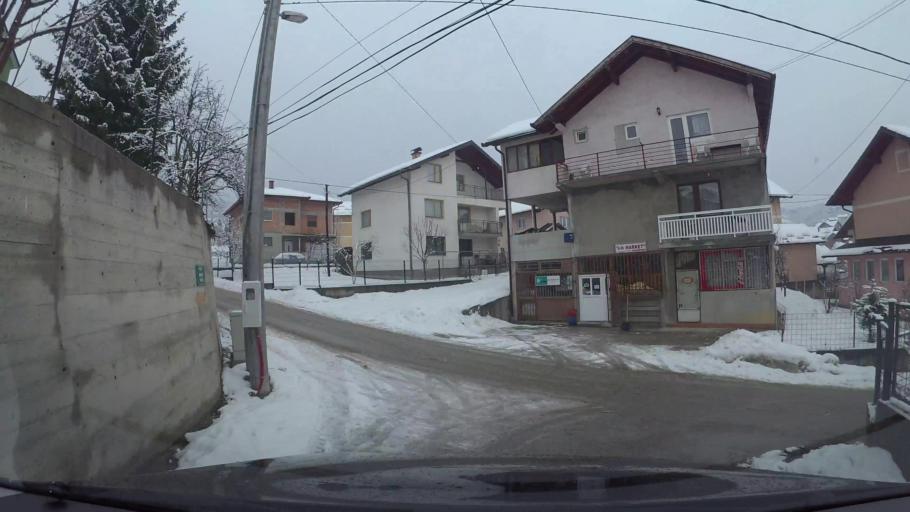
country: BA
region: Federation of Bosnia and Herzegovina
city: Vogosca
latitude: 43.8753
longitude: 18.3208
